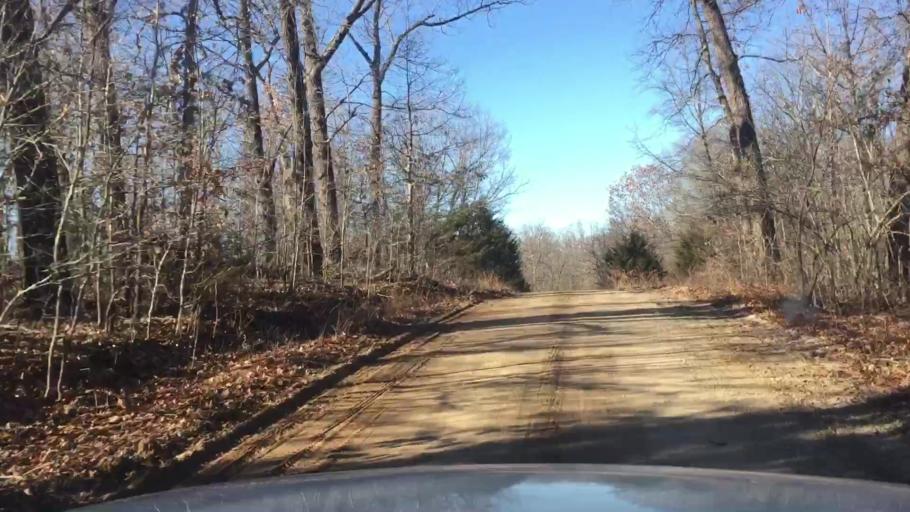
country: US
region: Missouri
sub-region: Camden County
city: Four Seasons
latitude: 38.3175
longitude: -92.7555
